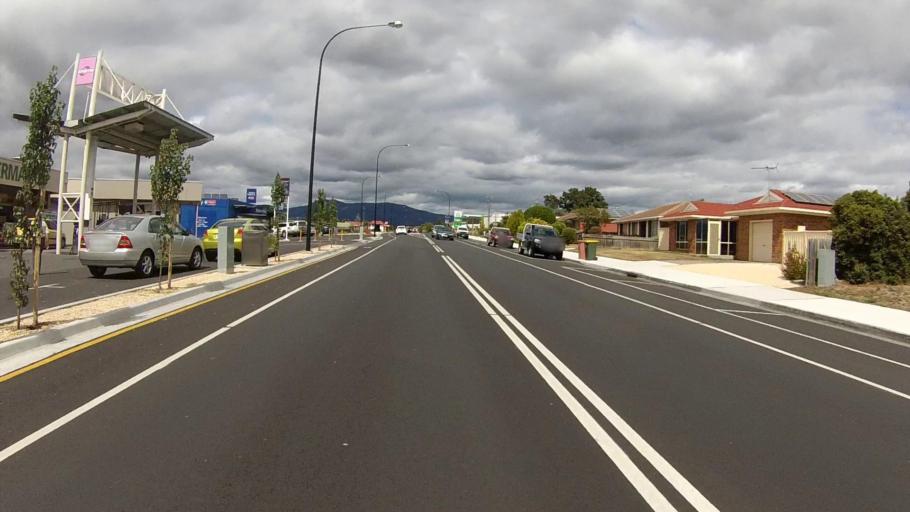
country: AU
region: Tasmania
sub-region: Brighton
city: Bridgewater
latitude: -42.6978
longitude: 147.2531
